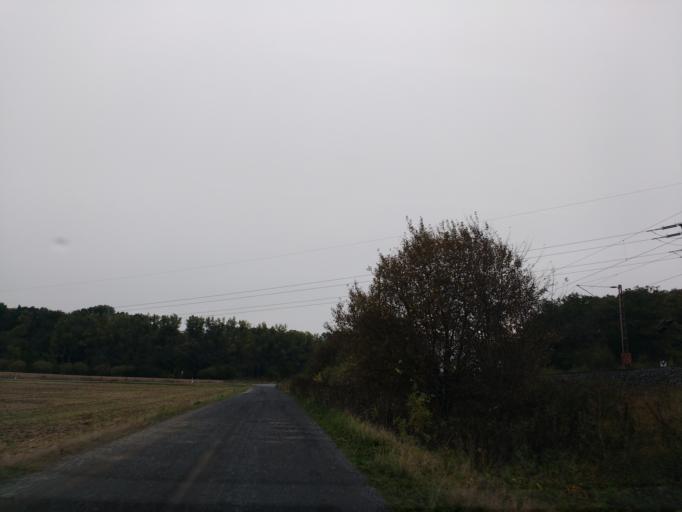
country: DE
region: Lower Saxony
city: Gemeinde Friedland
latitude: 51.4083
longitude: 9.9143
